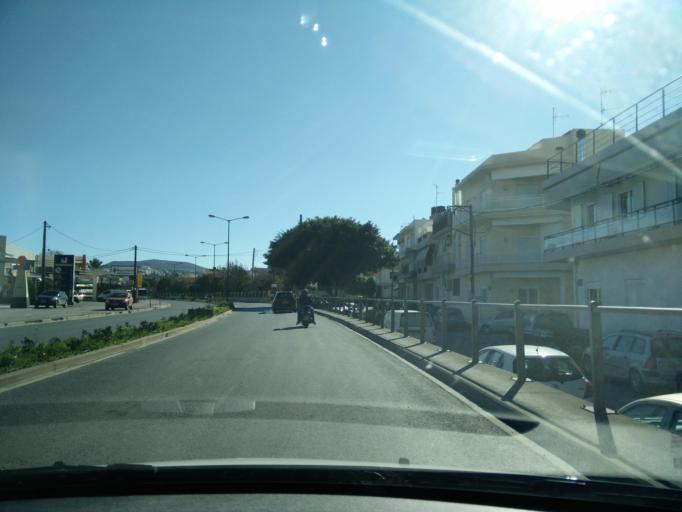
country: GR
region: Crete
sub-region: Nomos Irakleiou
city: Nea Alikarnassos
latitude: 35.3384
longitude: 25.1537
